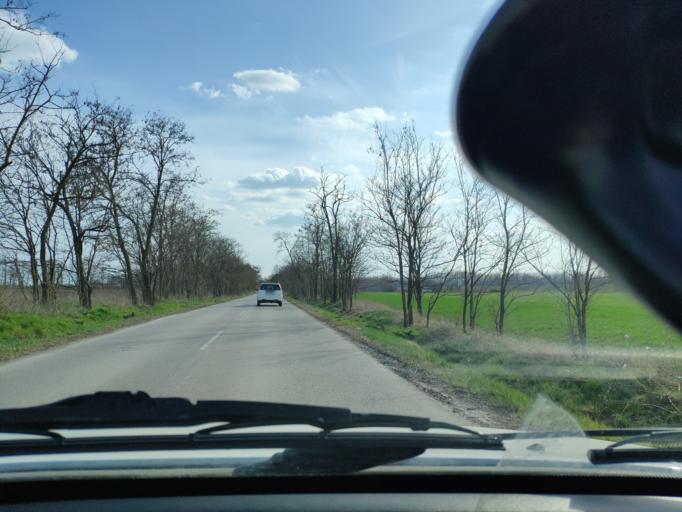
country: HU
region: Fejer
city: Adony
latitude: 47.1237
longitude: 18.8971
